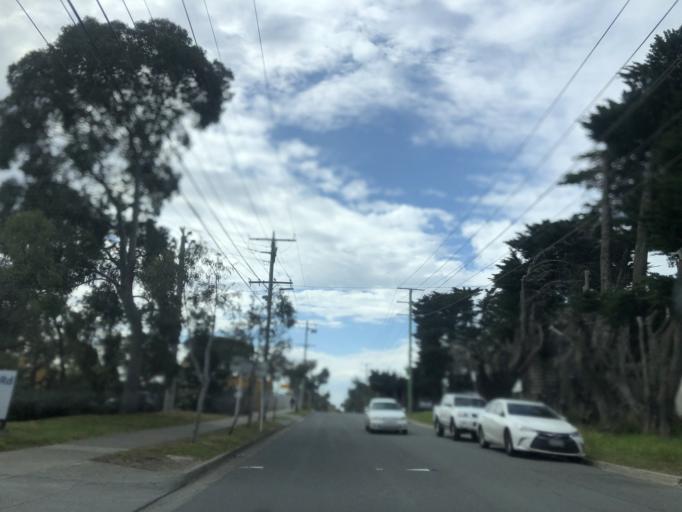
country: AU
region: Victoria
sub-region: Monash
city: Notting Hill
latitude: -37.9141
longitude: 145.1499
